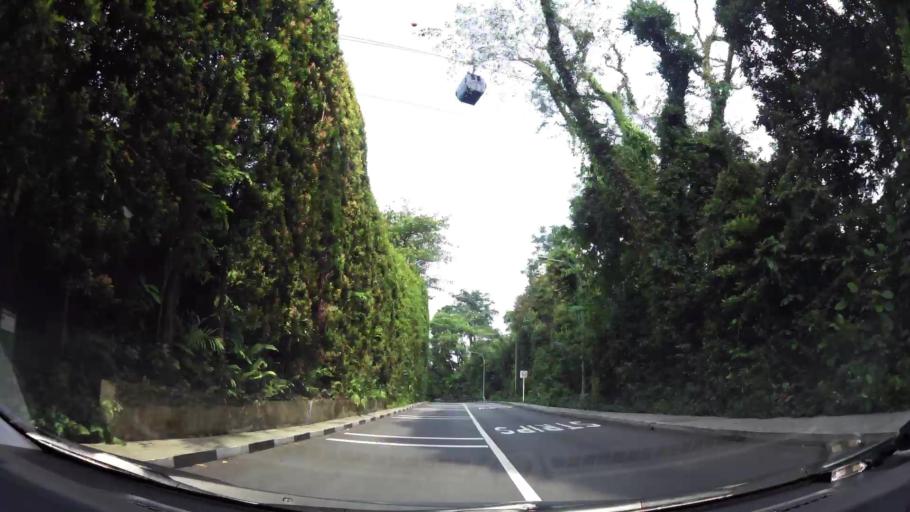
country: SG
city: Singapore
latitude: 1.2561
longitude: 103.8179
